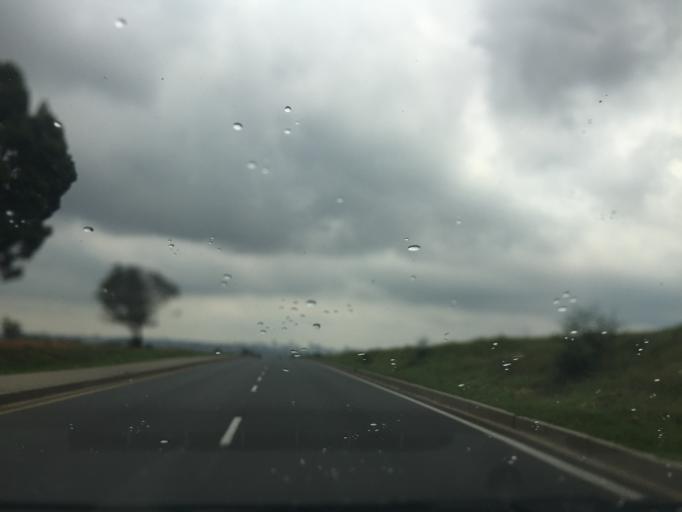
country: ZA
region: Gauteng
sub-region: City of Johannesburg Metropolitan Municipality
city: Modderfontein
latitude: -26.1048
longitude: 28.1321
